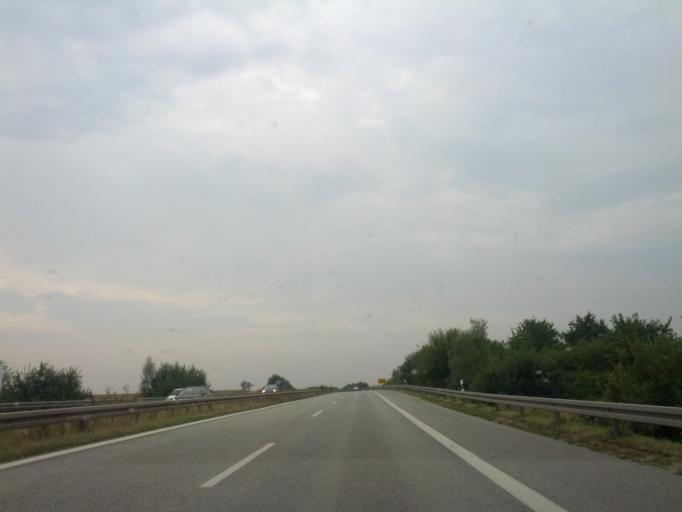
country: DE
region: Mecklenburg-Vorpommern
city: Kritzmow
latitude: 54.0581
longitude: 12.0409
